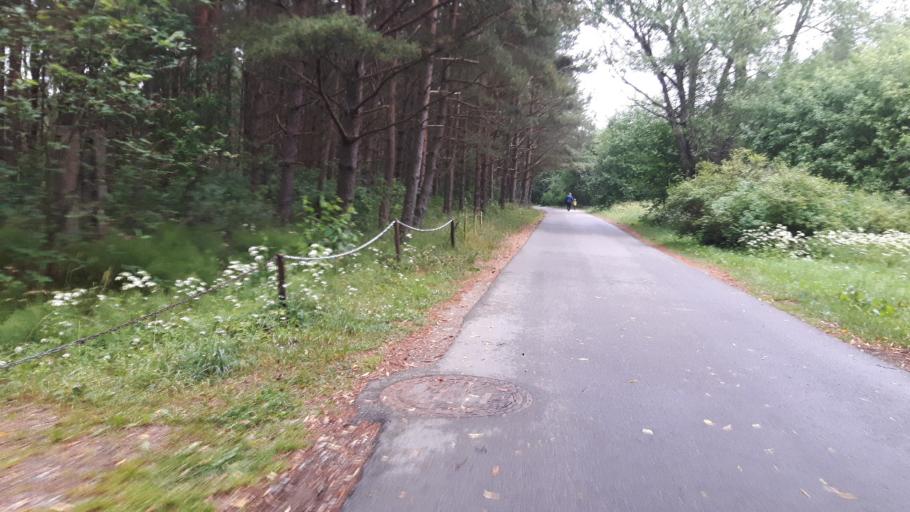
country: LT
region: Klaipedos apskritis
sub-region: Palanga
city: Sventoji
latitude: 56.0058
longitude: 21.0757
